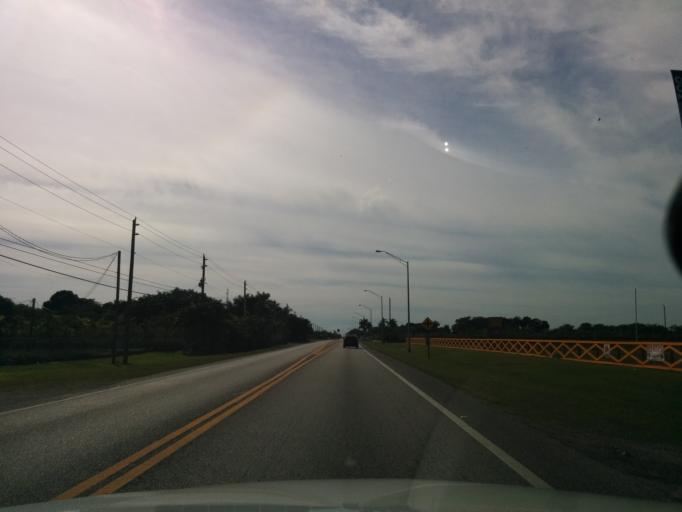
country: US
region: Florida
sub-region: Miami-Dade County
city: Naranja
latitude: 25.5318
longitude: -80.4780
